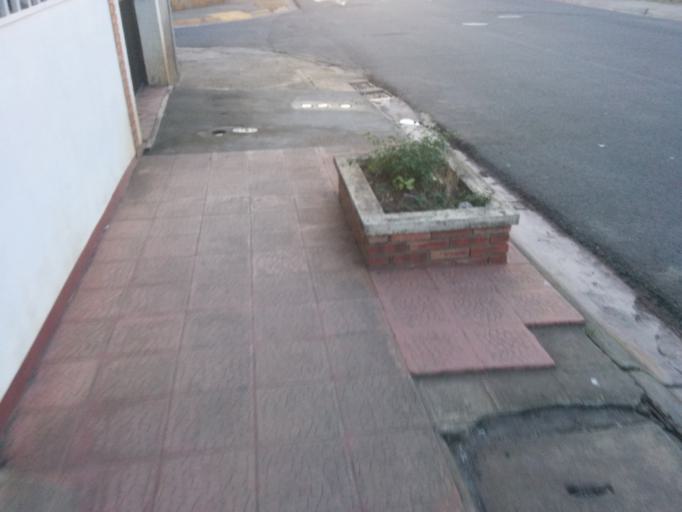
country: CR
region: Heredia
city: Llorente
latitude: 9.9929
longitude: -84.1502
